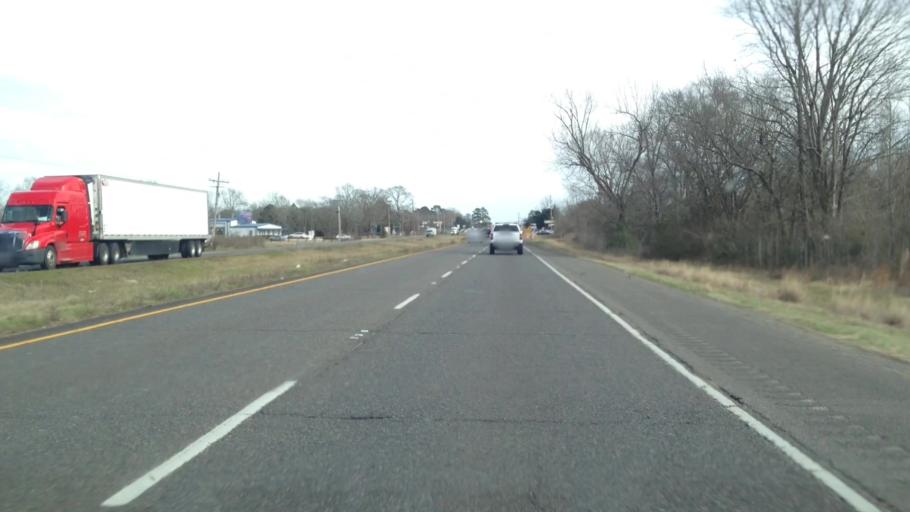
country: US
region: Louisiana
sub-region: Saint Landry Parish
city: Port Barre
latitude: 30.5472
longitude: -91.9768
